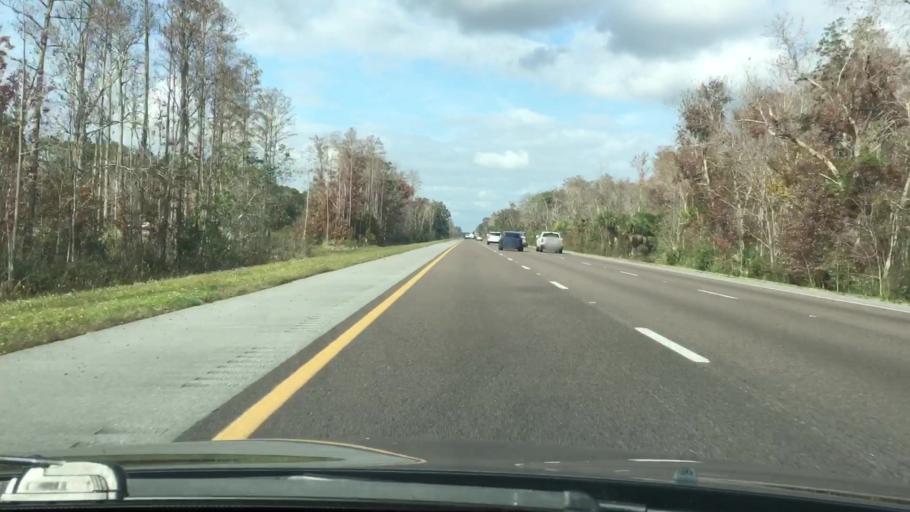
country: US
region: Florida
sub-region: Volusia County
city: Oak Hill
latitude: 28.8759
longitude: -80.9213
